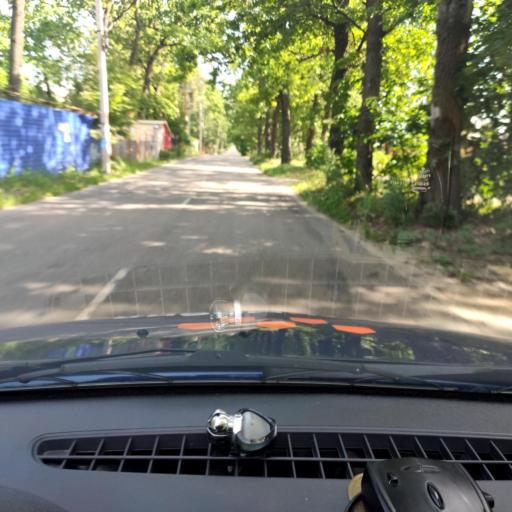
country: RU
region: Voronezj
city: Somovo
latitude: 51.7496
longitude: 39.3661
